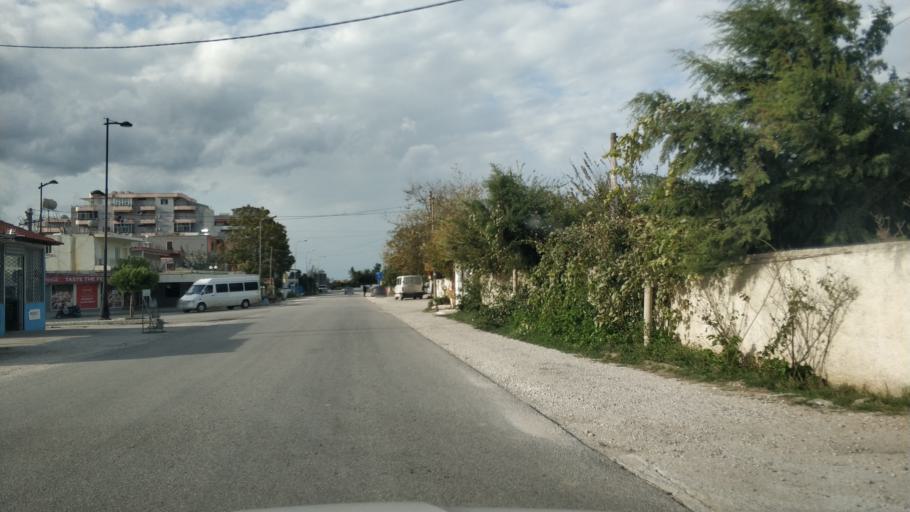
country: AL
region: Vlore
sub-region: Rrethi i Vlores
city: Orikum
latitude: 40.3298
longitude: 19.4776
